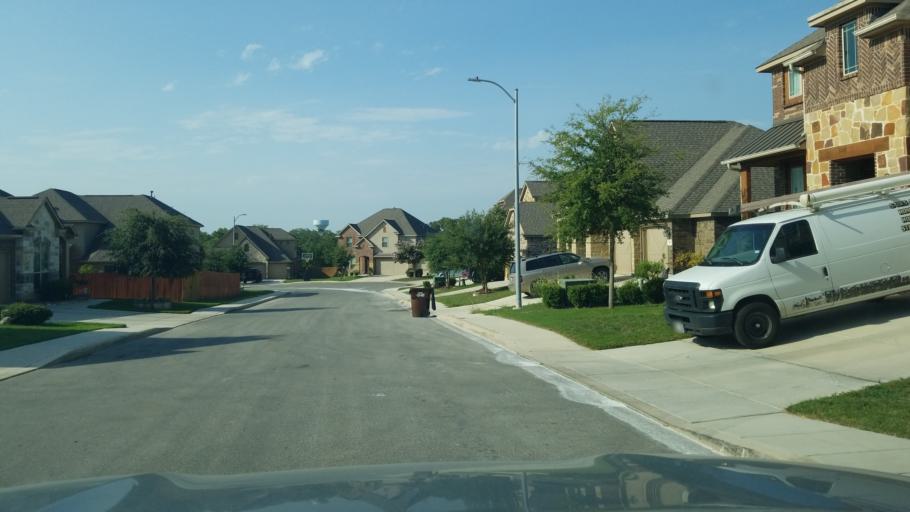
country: US
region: Texas
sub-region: Medina County
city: La Coste
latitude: 29.4381
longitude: -98.7534
